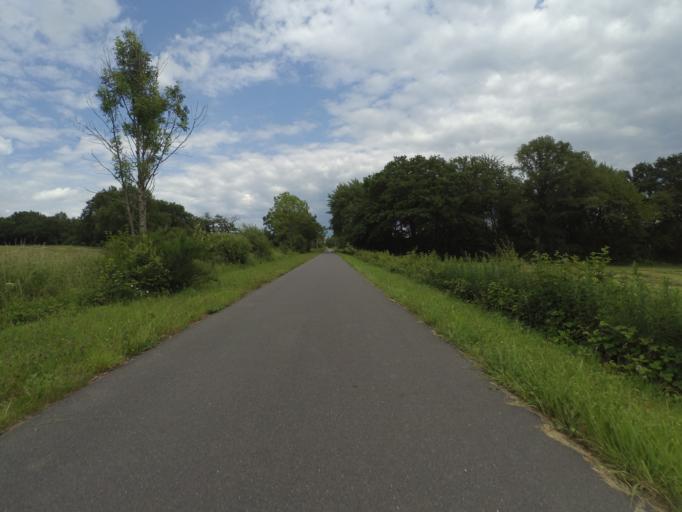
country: DE
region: North Rhine-Westphalia
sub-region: Regierungsbezirk Koln
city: Roetgen
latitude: 50.6553
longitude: 6.1927
